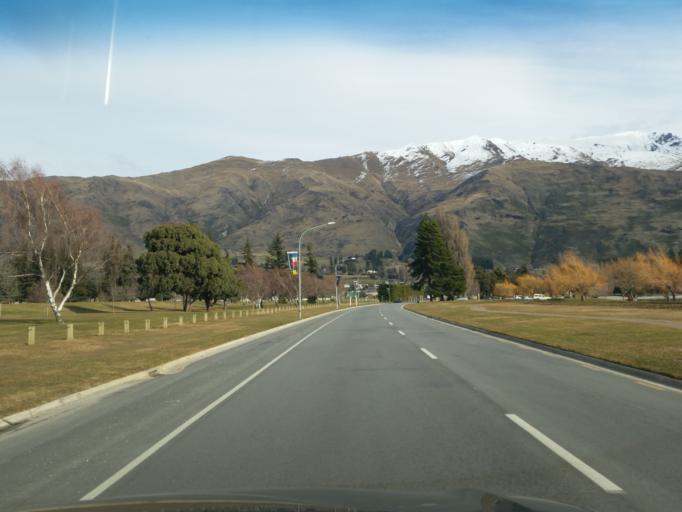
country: NZ
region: Otago
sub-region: Queenstown-Lakes District
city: Wanaka
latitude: -44.6973
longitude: 169.1307
